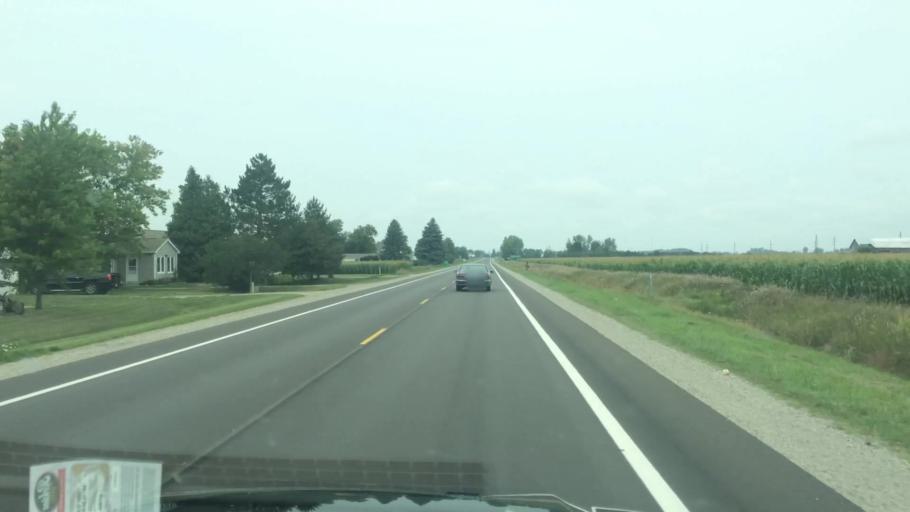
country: US
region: Michigan
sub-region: Huron County
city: Bad Axe
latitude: 43.9927
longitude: -83.0074
